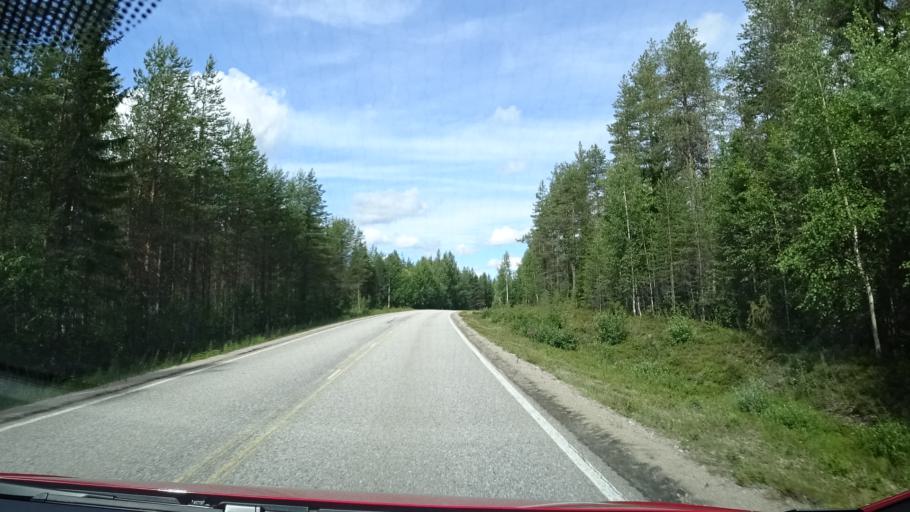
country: FI
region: Kainuu
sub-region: Kehys-Kainuu
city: Kuhmo
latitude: 64.4476
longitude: 29.7893
